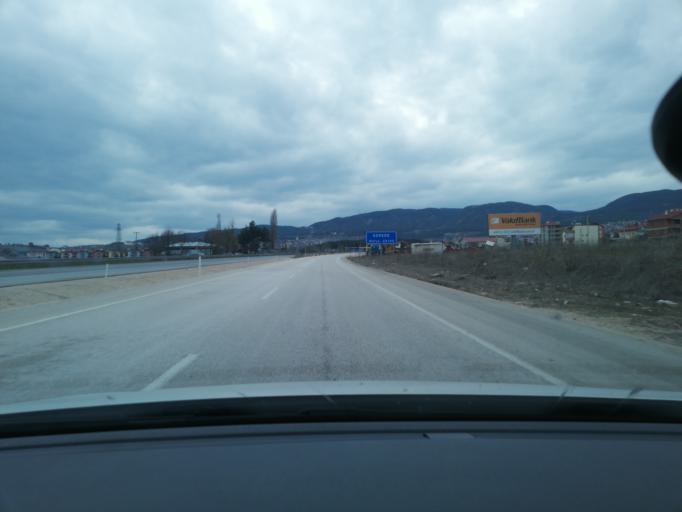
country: TR
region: Bolu
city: Gerede
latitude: 40.7822
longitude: 32.2131
